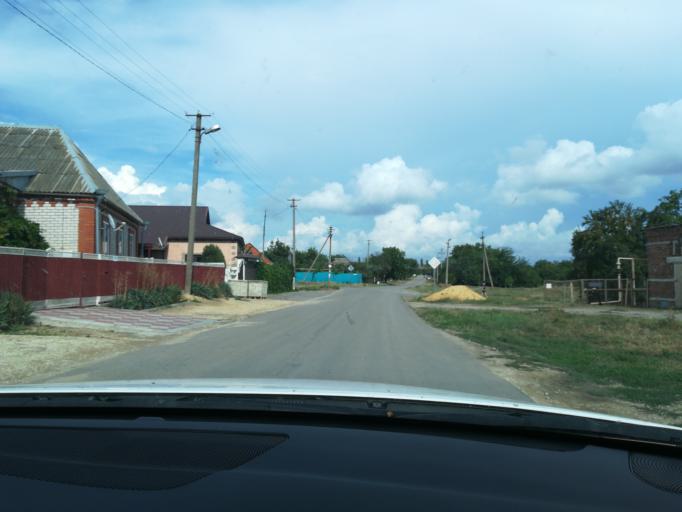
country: RU
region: Krasnodarskiy
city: Strelka
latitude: 45.1712
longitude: 37.2731
